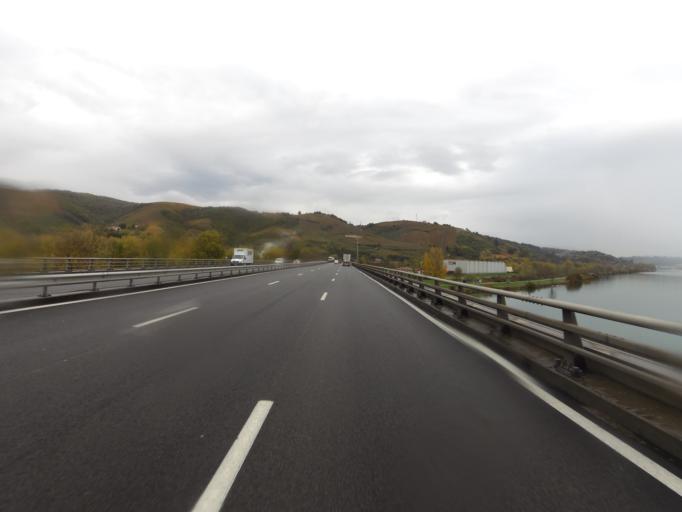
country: FR
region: Rhone-Alpes
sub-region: Departement du Rhone
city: Saint-Cyr-sur-le-Rhone
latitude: 45.5004
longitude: 4.8392
